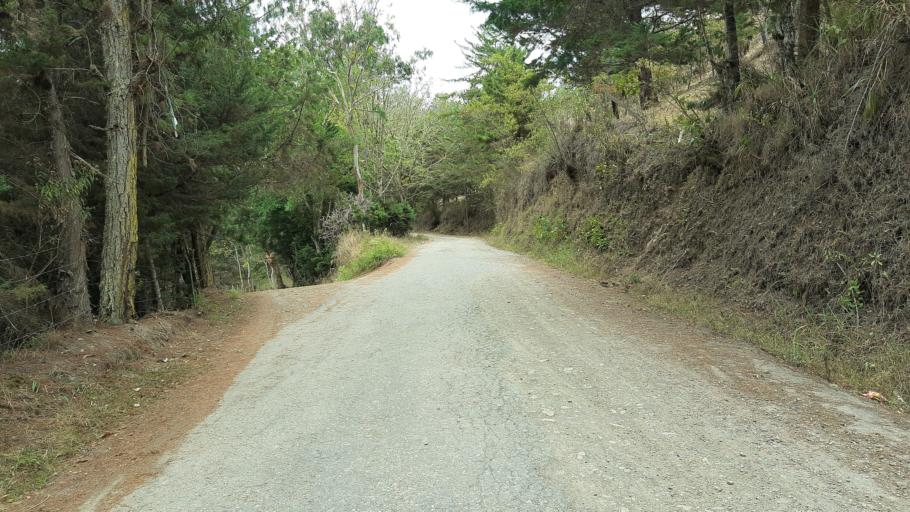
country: CO
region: Boyaca
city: Somondoco
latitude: 4.9750
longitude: -73.3799
